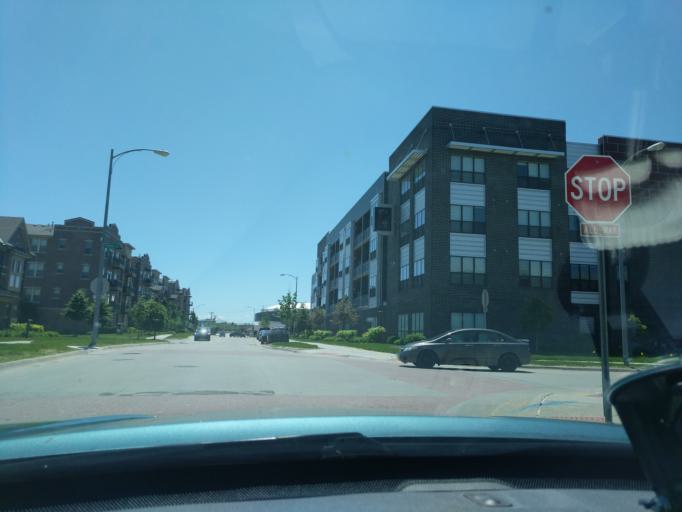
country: US
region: Nebraska
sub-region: Douglas County
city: Ralston
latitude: 41.2400
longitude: -96.0120
